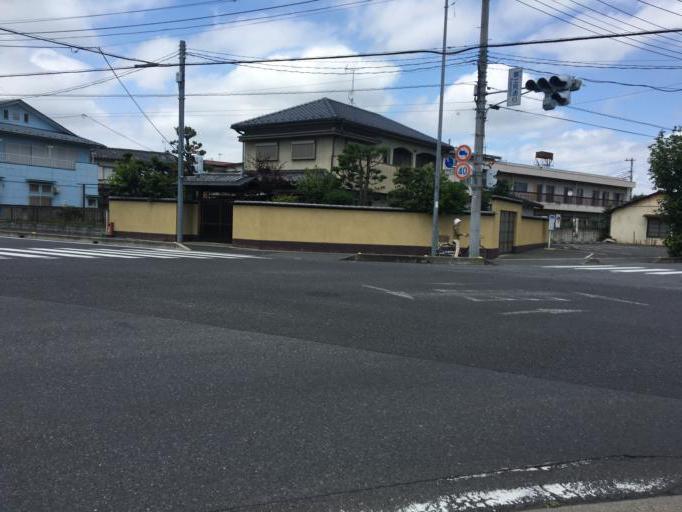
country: JP
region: Saitama
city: Okegawa
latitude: 35.9957
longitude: 139.5708
